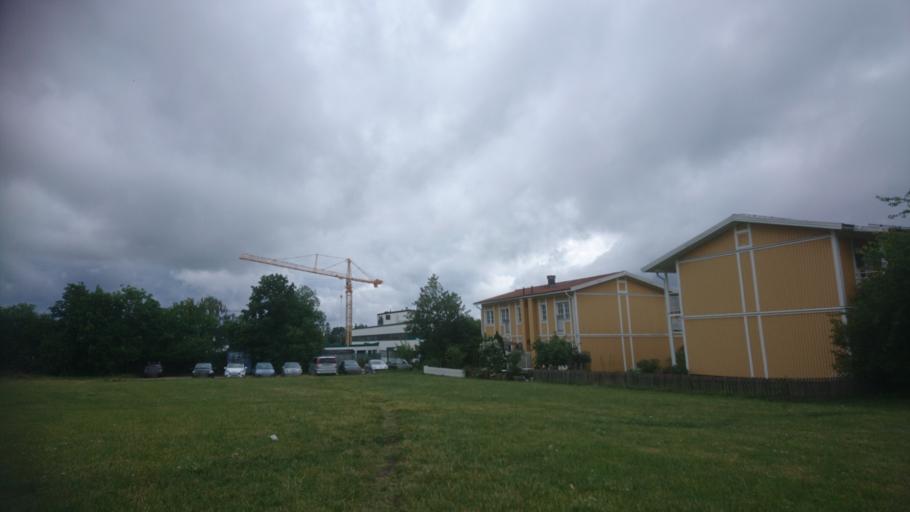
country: SE
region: Stockholm
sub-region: Upplands Vasby Kommun
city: Upplands Vaesby
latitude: 59.5172
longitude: 17.8925
